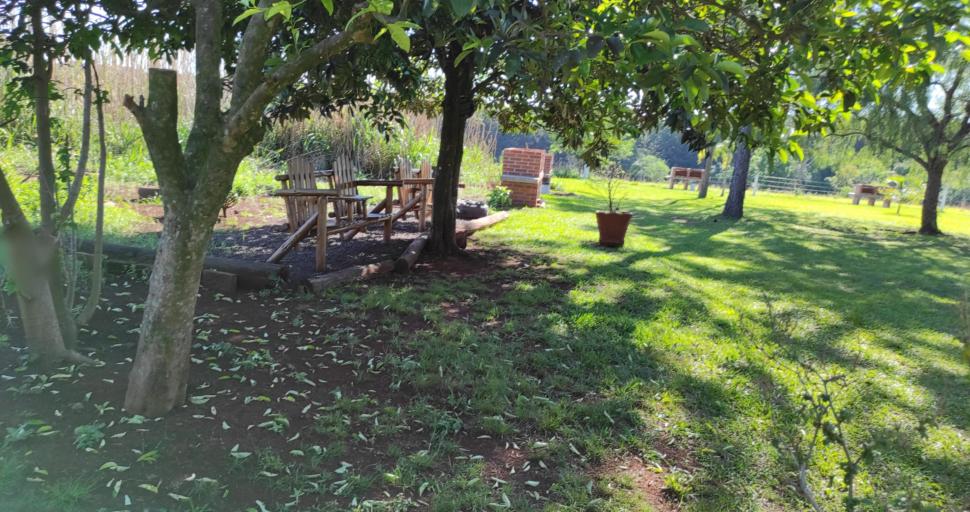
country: AR
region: Misiones
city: Capiovi
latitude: -26.9150
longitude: -55.0947
